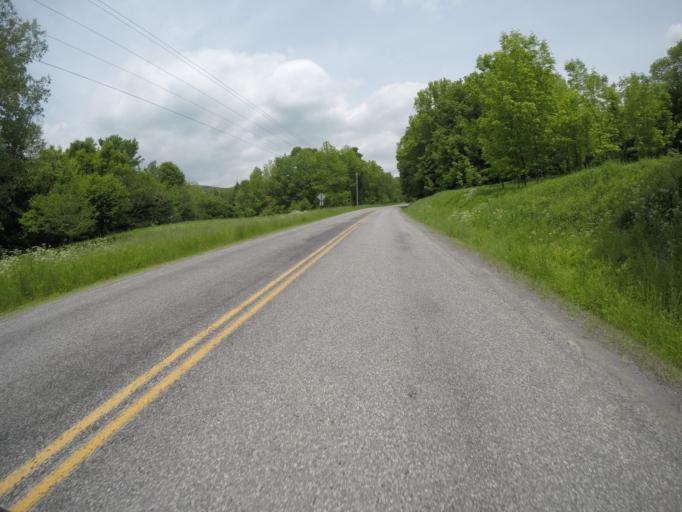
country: US
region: New York
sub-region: Delaware County
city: Stamford
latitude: 42.1784
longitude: -74.6740
